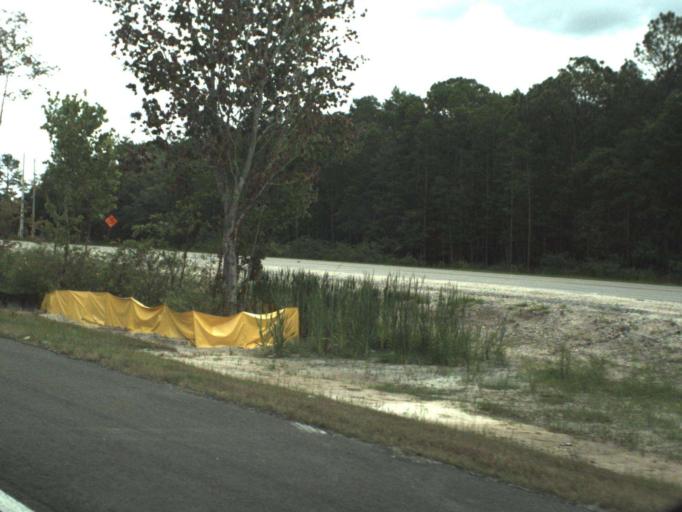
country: US
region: Florida
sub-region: Volusia County
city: Lake Helen
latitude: 29.0621
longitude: -81.1898
